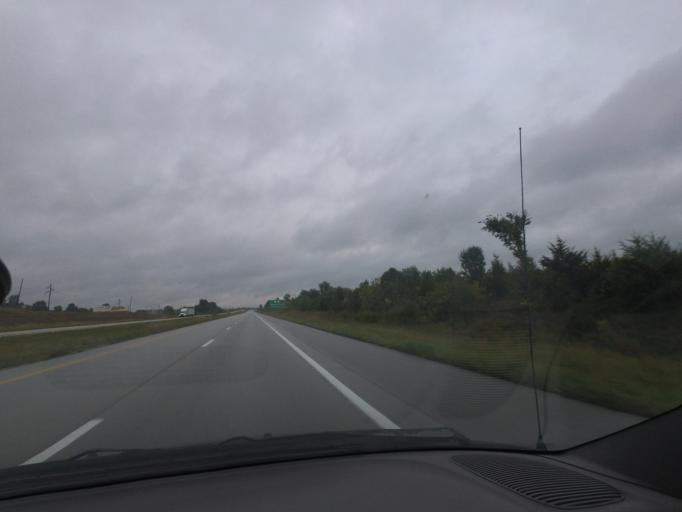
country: US
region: Missouri
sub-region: Marion County
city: Monroe City
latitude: 39.6646
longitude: -91.7326
